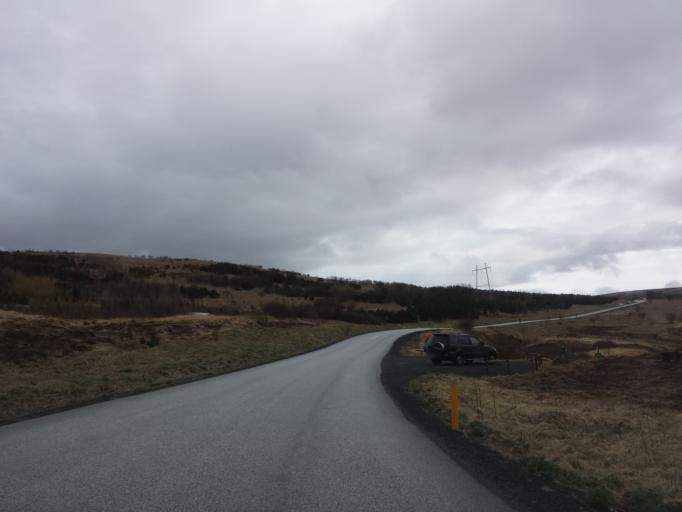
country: IS
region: Capital Region
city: Kopavogur
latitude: 64.0825
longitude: -21.8690
